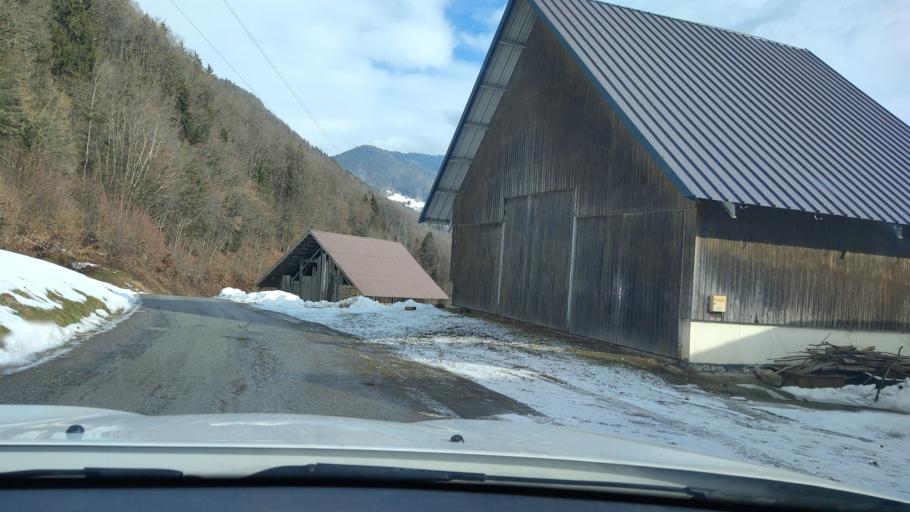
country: FR
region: Rhone-Alpes
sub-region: Departement de la Savoie
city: Marthod
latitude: 45.7009
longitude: 6.4236
